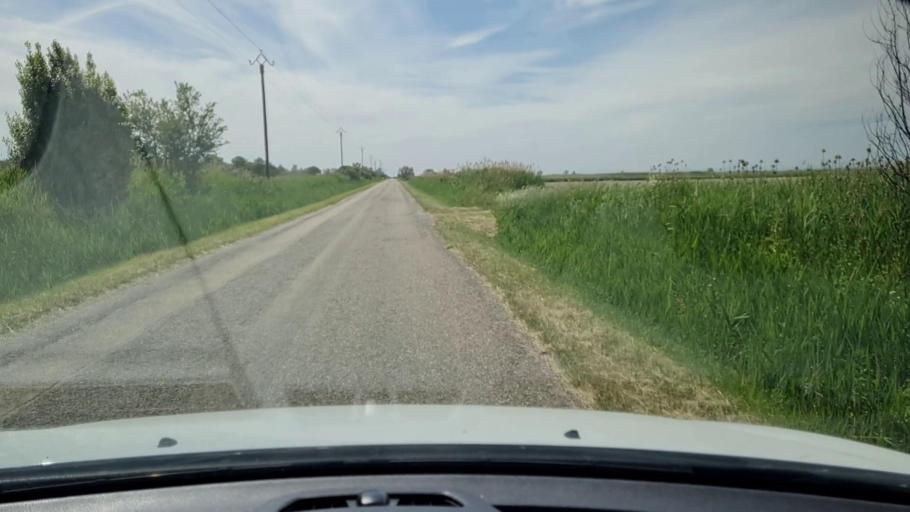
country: FR
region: Languedoc-Roussillon
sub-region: Departement du Gard
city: Saint-Gilles
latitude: 43.5895
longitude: 4.4386
